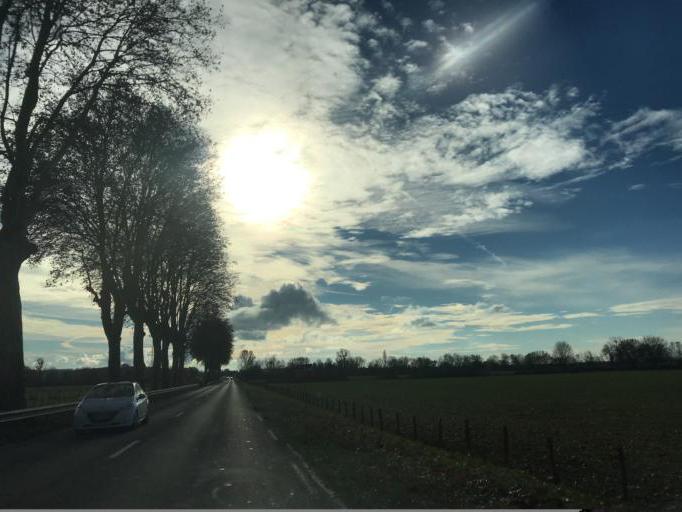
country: FR
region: Rhone-Alpes
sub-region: Departement de l'Ain
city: Ambronay
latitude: 45.9919
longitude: 5.3527
